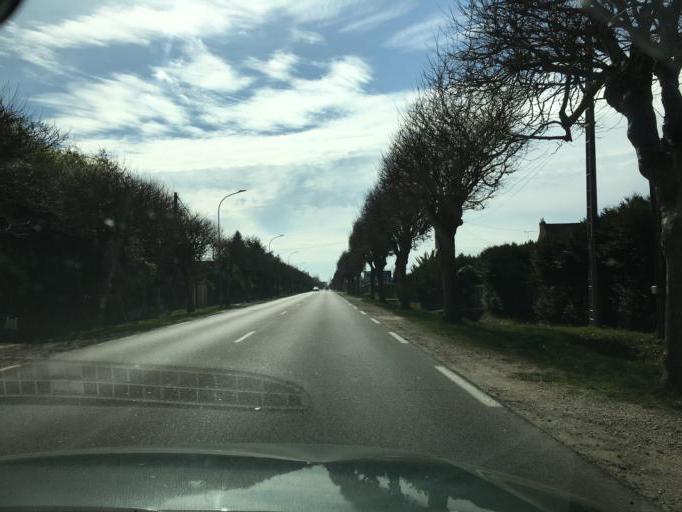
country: FR
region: Centre
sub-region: Departement du Loiret
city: Chateauneuf-sur-Loire
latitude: 47.8770
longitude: 2.2310
